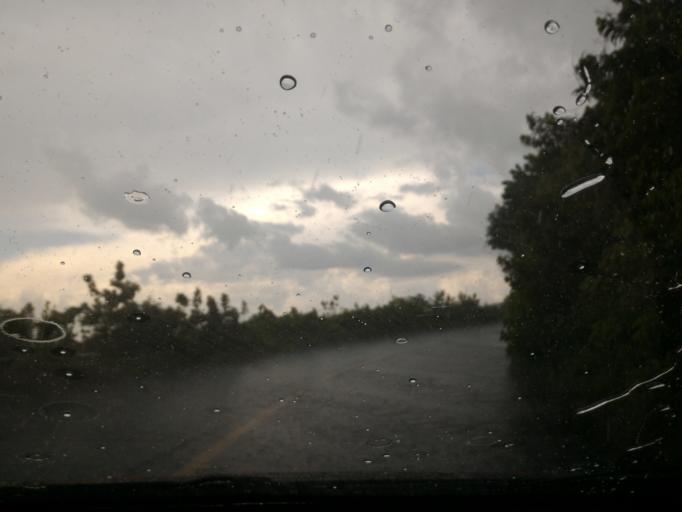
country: MX
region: Jalisco
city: San Andres Ixtlan
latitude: 19.8306
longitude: -103.4627
